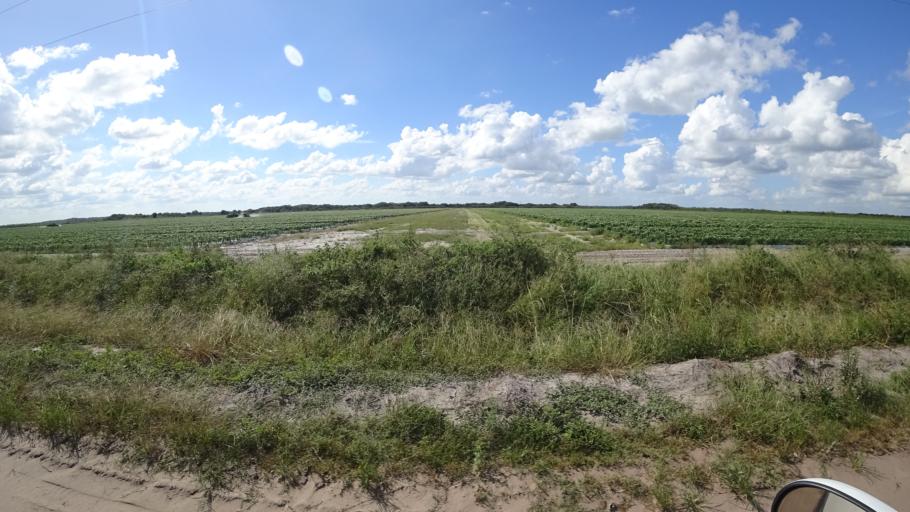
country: US
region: Florida
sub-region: DeSoto County
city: Arcadia
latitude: 27.3366
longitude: -82.0969
